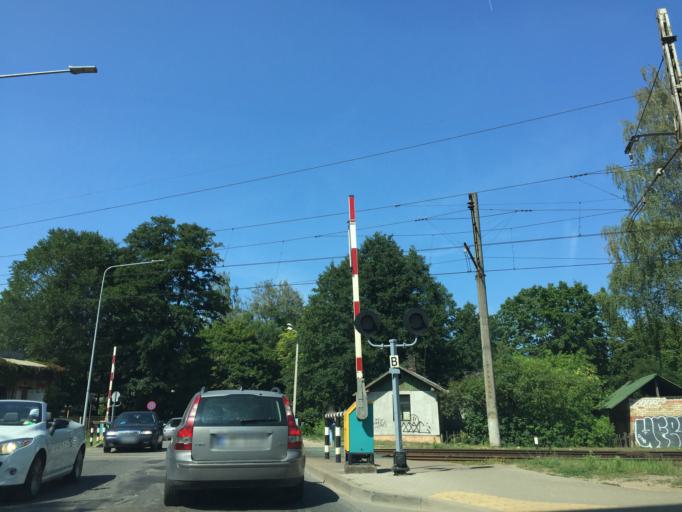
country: LV
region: Marupe
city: Marupe
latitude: 56.9501
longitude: 23.9982
